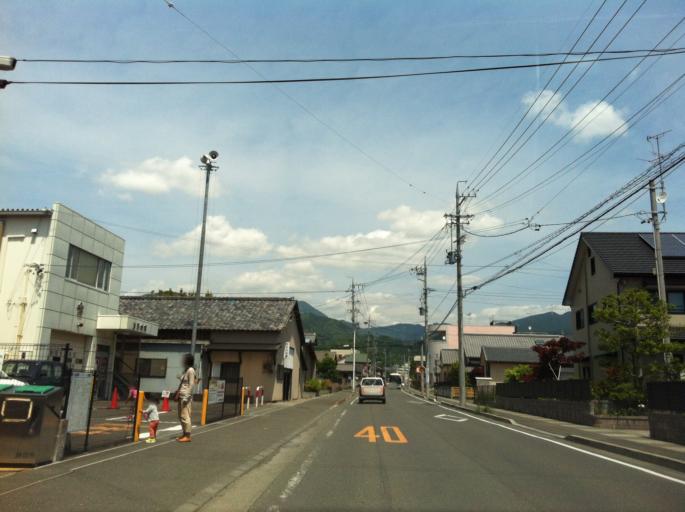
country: JP
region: Shizuoka
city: Shizuoka-shi
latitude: 35.0177
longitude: 138.4232
